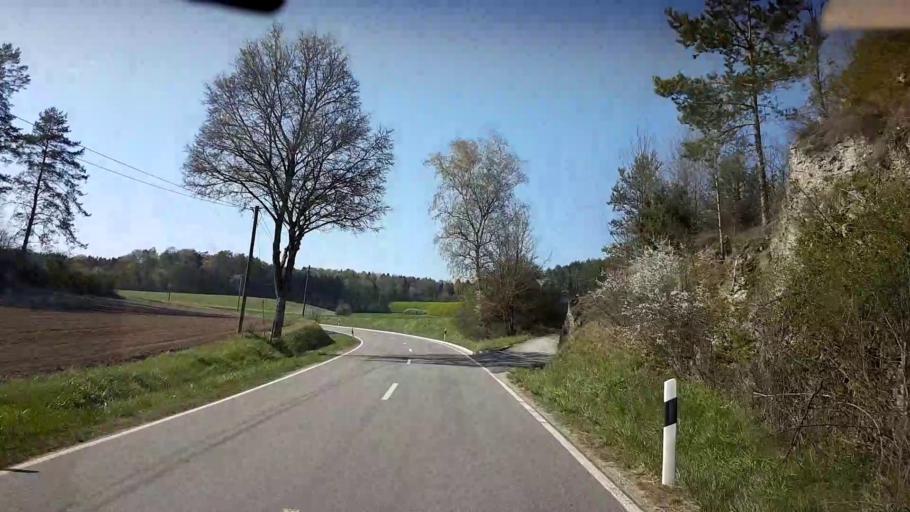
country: DE
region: Bavaria
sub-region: Upper Franconia
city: Pottenstein
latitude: 49.7901
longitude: 11.4200
